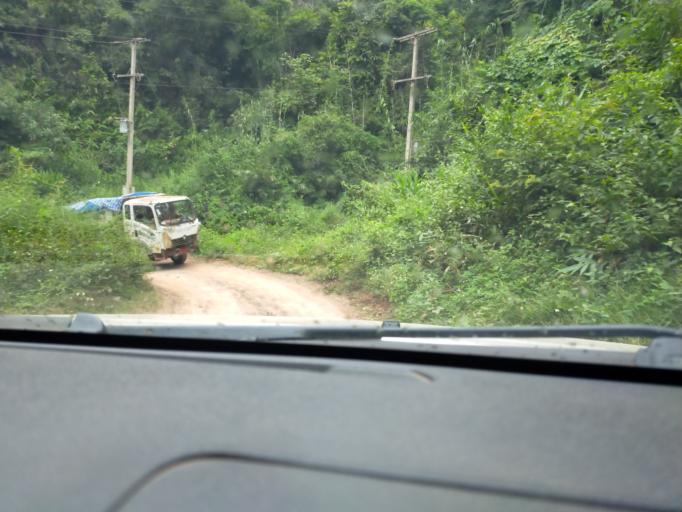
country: TH
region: Nan
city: Chaloem Phra Kiat
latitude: 19.8131
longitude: 101.3601
